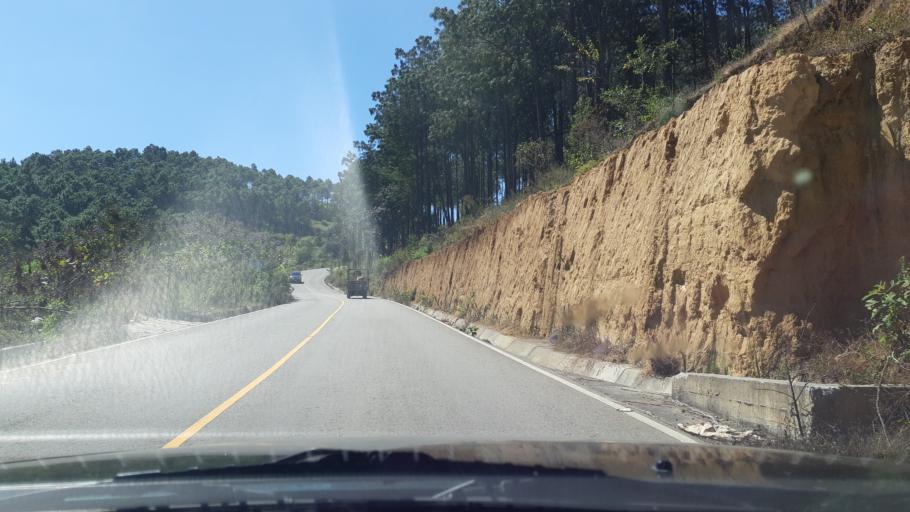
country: GT
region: Chimaltenango
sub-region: Municipio de Zaragoza
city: Zaragoza
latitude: 14.6665
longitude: -90.8584
